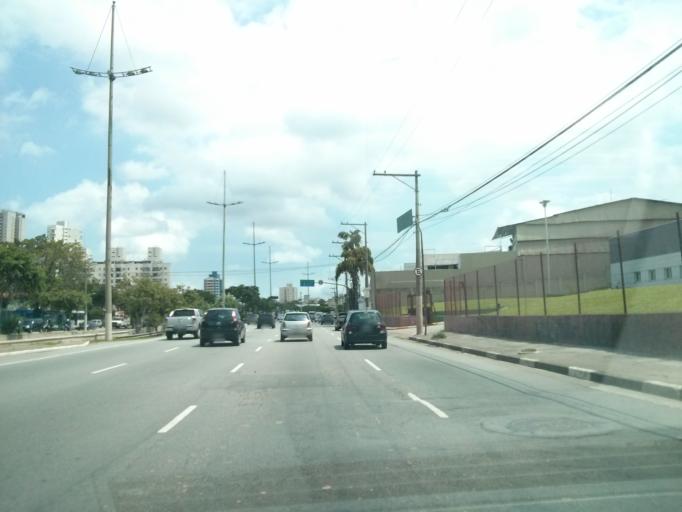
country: BR
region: Sao Paulo
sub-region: Diadema
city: Diadema
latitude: -23.6200
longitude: -46.6281
